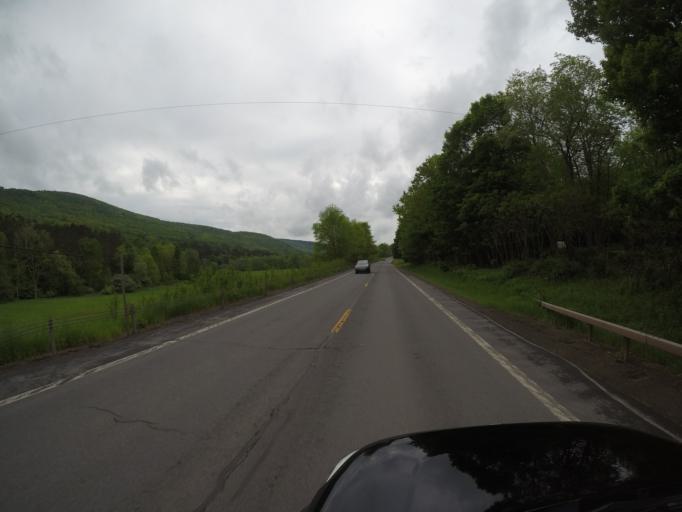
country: US
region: New York
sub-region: Delaware County
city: Delhi
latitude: 42.2547
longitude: -74.9065
